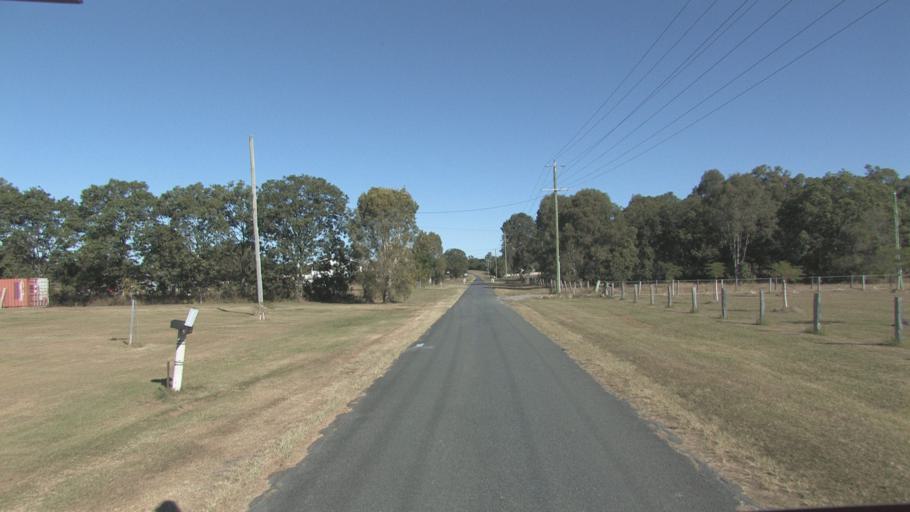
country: AU
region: Queensland
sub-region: Logan
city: North Maclean
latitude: -27.7785
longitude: 153.0194
